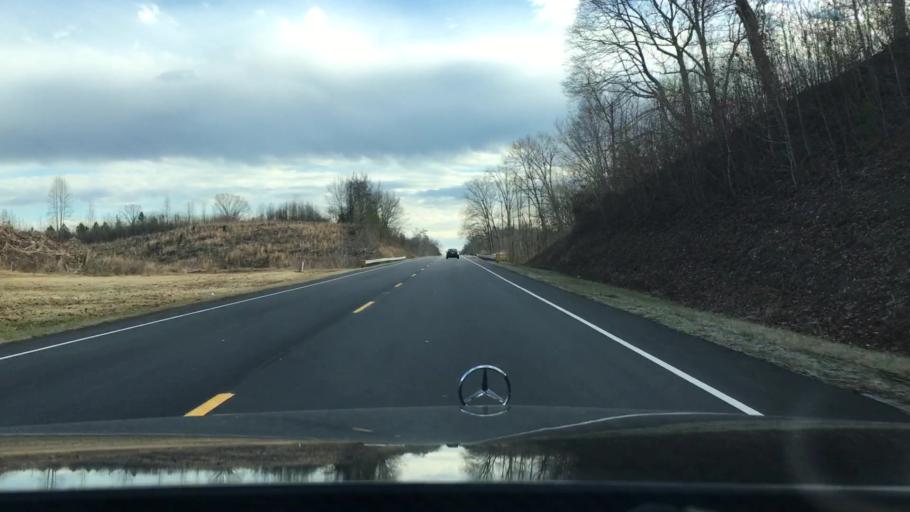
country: US
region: Virginia
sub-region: City of Danville
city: Danville
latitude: 36.5031
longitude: -79.3883
